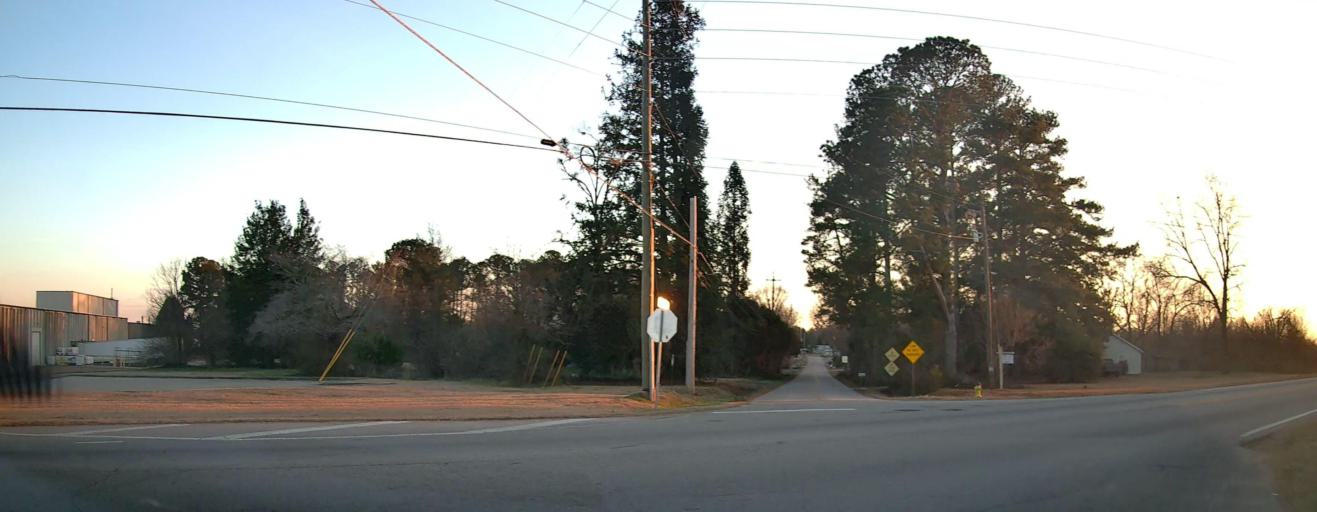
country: US
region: Georgia
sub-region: Troup County
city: La Grange
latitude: 33.0165
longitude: -85.0058
